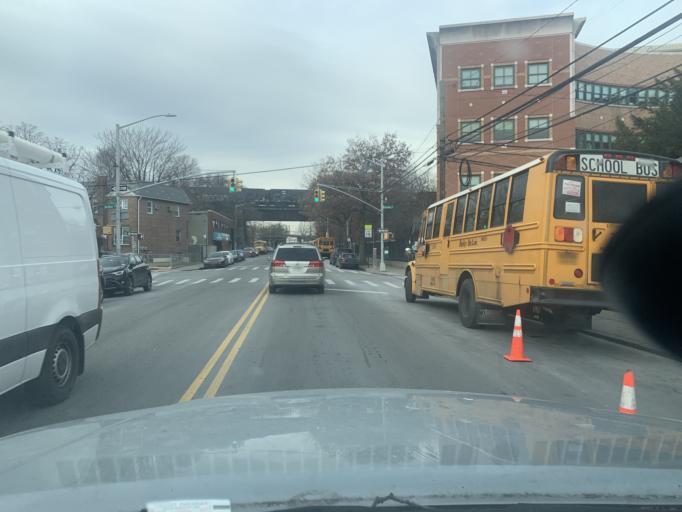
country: US
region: New York
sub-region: Queens County
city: Long Island City
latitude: 40.7369
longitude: -73.8871
